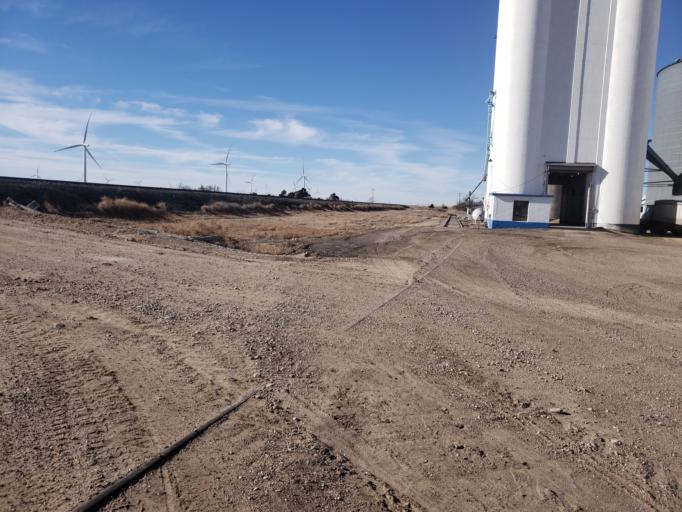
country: US
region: Kansas
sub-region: Edwards County
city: Kinsley
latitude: 37.8728
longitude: -99.6577
